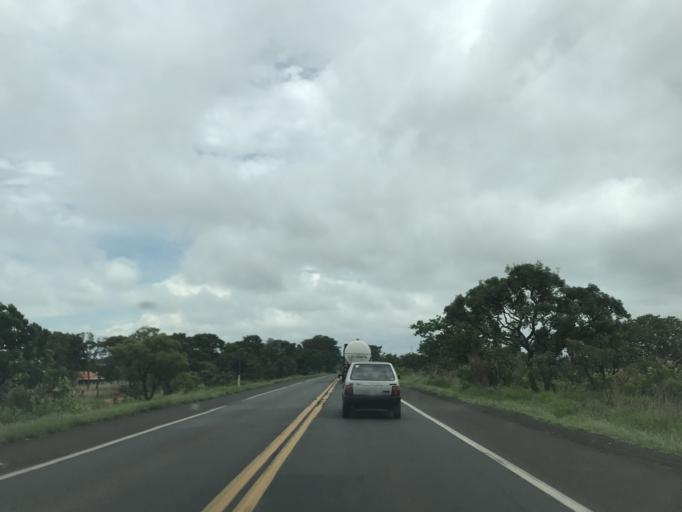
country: BR
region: Minas Gerais
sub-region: Frutal
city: Frutal
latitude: -19.8077
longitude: -48.9678
